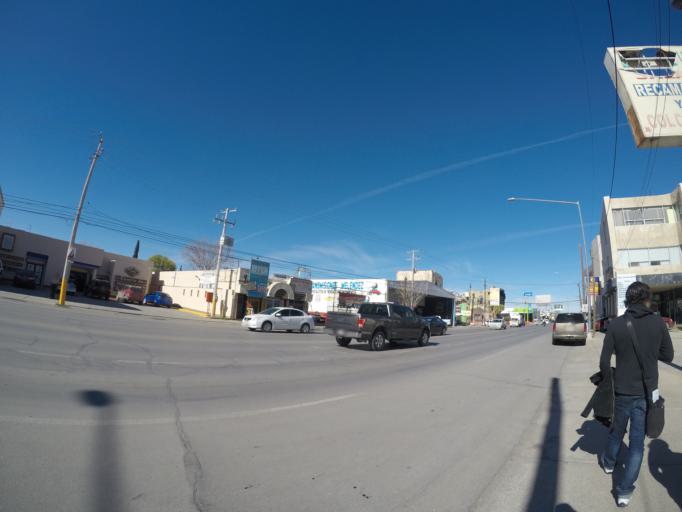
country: MX
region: Chihuahua
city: Ciudad Juarez
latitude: 31.7424
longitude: -106.4572
